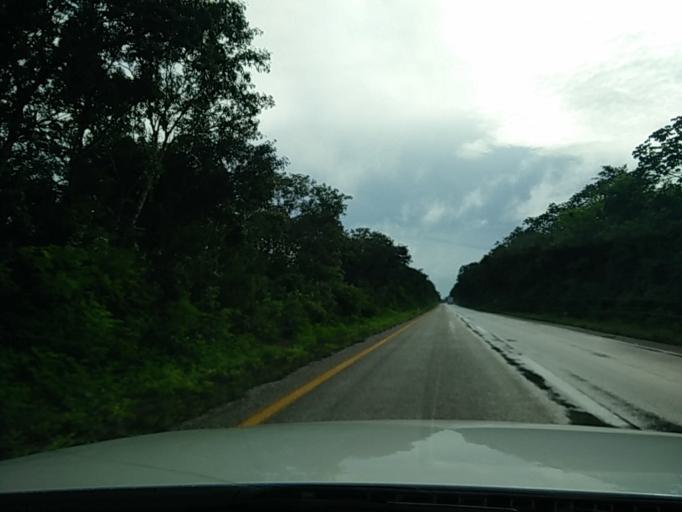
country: MX
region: Yucatan
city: Tunkas
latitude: 20.7534
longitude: -88.7368
